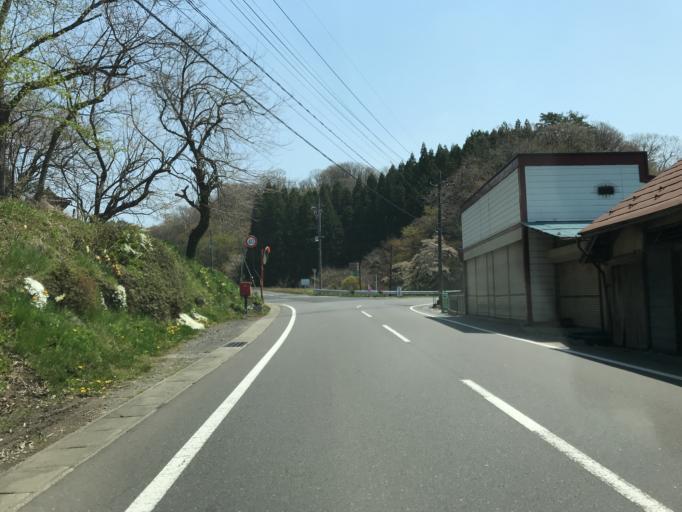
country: JP
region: Fukushima
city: Ishikawa
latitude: 37.0620
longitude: 140.4548
